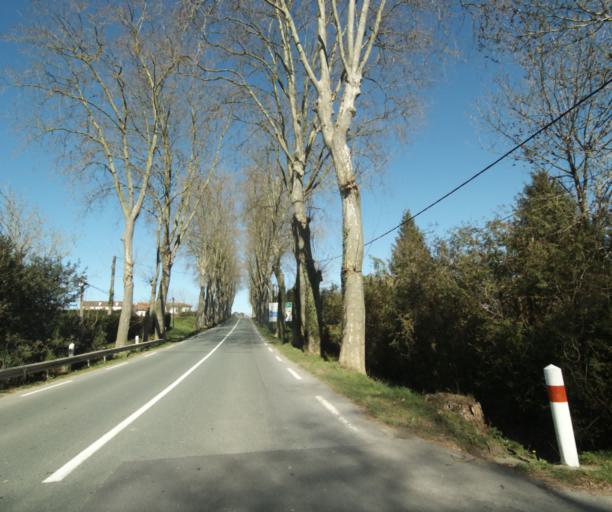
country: FR
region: Aquitaine
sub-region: Departement des Pyrenees-Atlantiques
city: Ciboure
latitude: 43.3700
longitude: -1.6828
